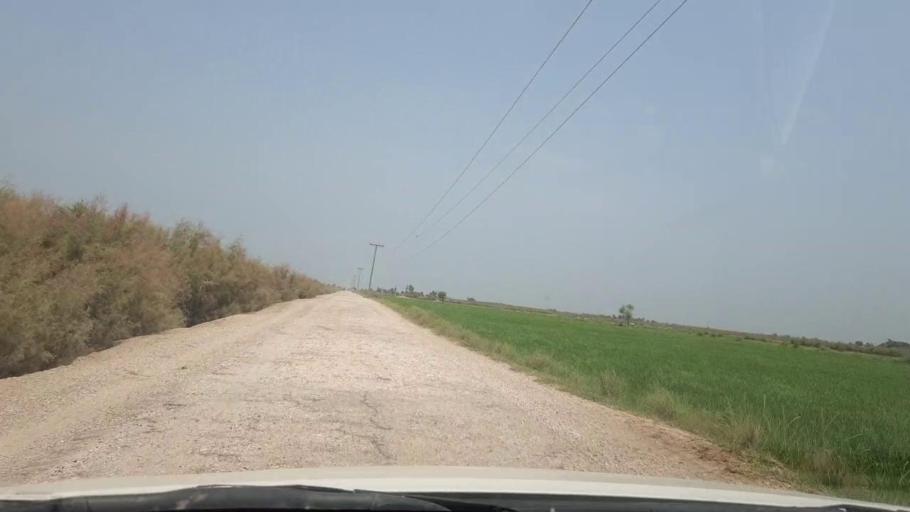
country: PK
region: Sindh
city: Rustam jo Goth
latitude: 28.0487
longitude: 68.8154
